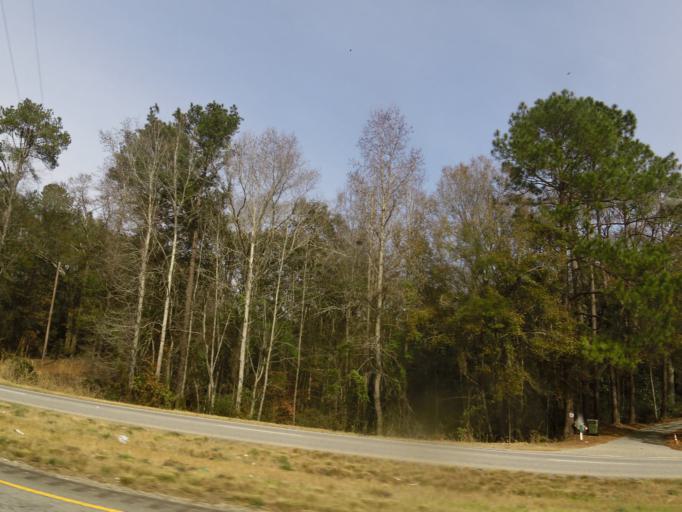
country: US
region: Alabama
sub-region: Dale County
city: Midland City
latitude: 31.3252
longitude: -85.5250
